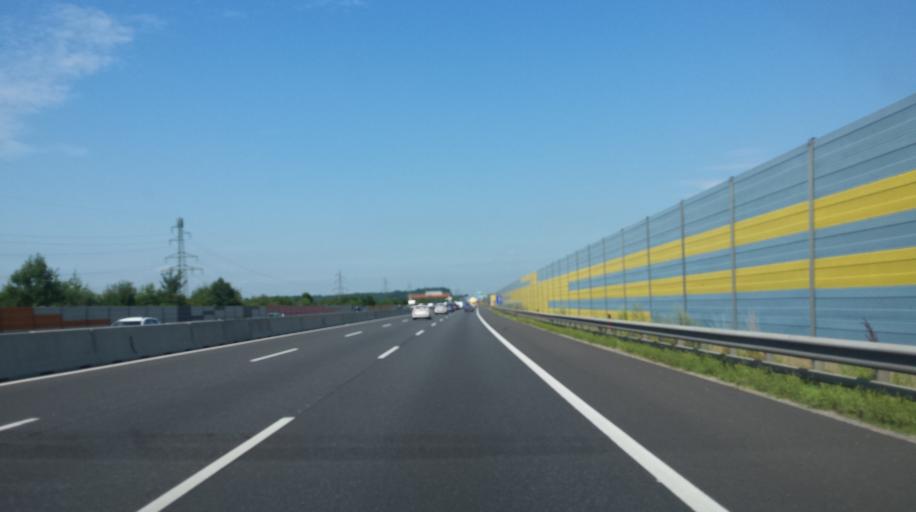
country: AT
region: Lower Austria
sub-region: Sankt Polten Stadt
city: Sankt Poelten
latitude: 48.1761
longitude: 15.6408
